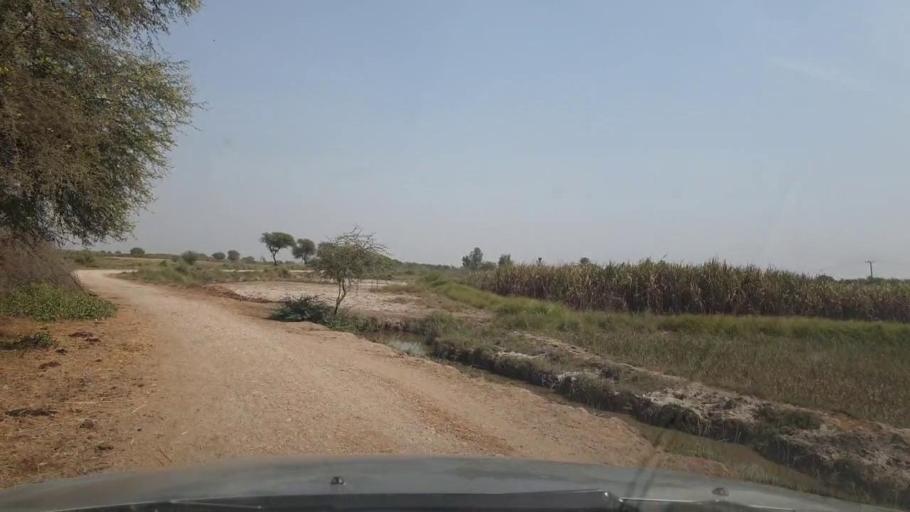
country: PK
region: Sindh
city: Bulri
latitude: 24.8833
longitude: 68.3982
